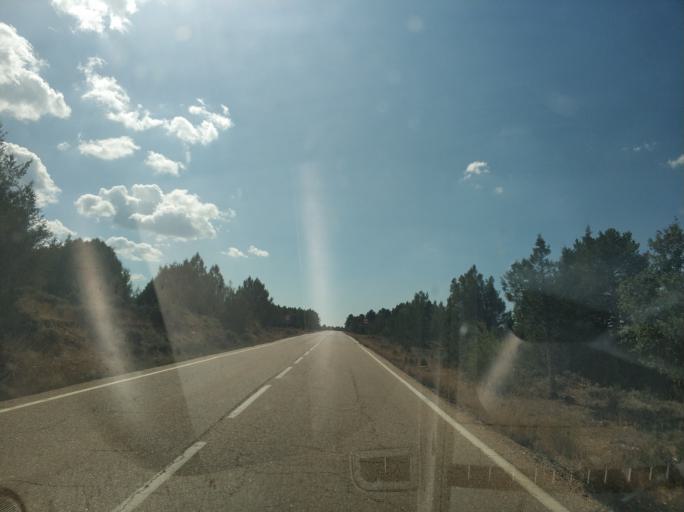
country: ES
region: Castille and Leon
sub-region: Provincia de Soria
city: Herrera de Soria
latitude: 41.7699
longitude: -3.0302
